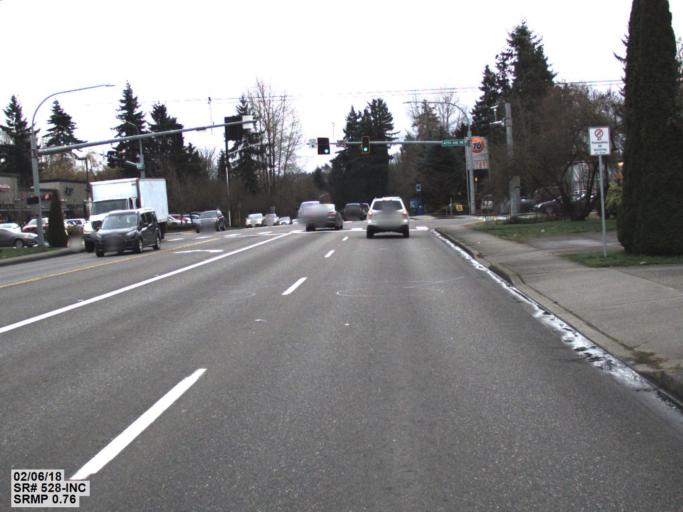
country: US
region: Washington
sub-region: Snohomish County
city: Marysville
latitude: 48.0518
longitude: -122.1684
